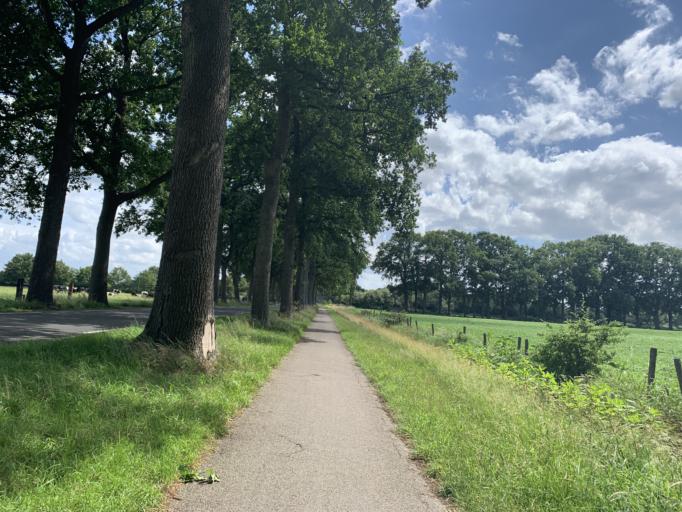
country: NL
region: Drenthe
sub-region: Gemeente Tynaarlo
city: Zuidlaren
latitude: 53.1379
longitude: 6.6533
